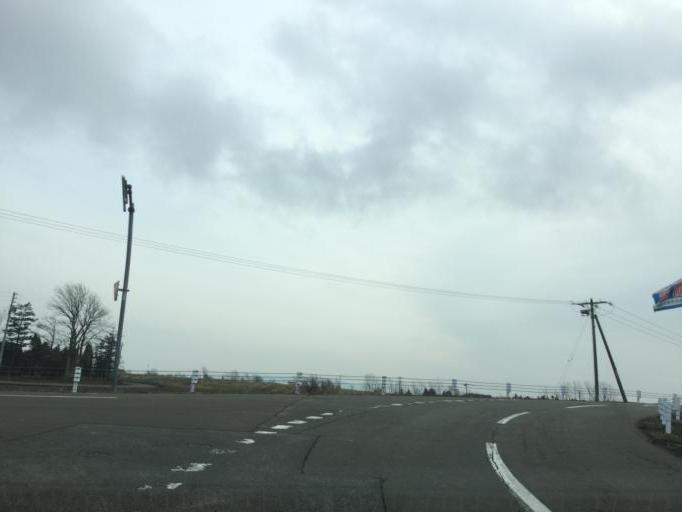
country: JP
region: Hokkaido
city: Iwamizawa
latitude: 43.1548
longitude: 141.6866
